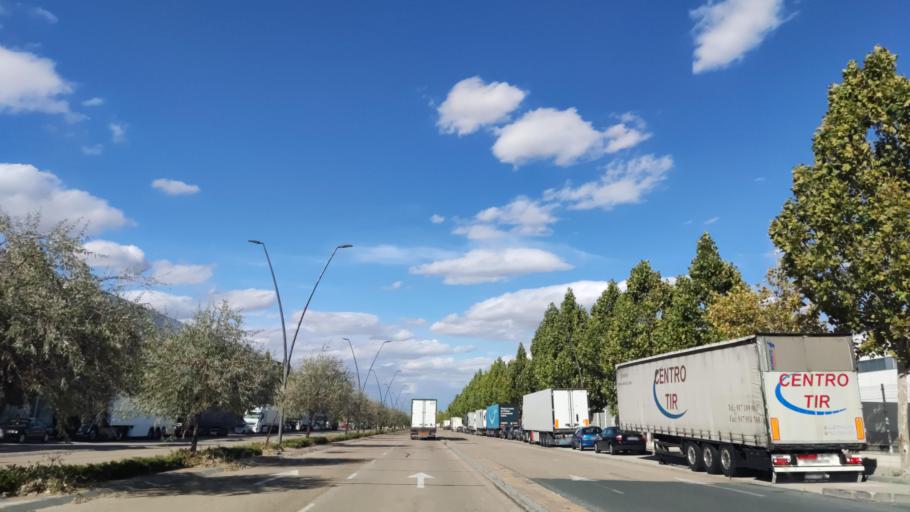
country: ES
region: Madrid
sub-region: Provincia de Madrid
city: Pinto
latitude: 40.2797
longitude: -3.6820
